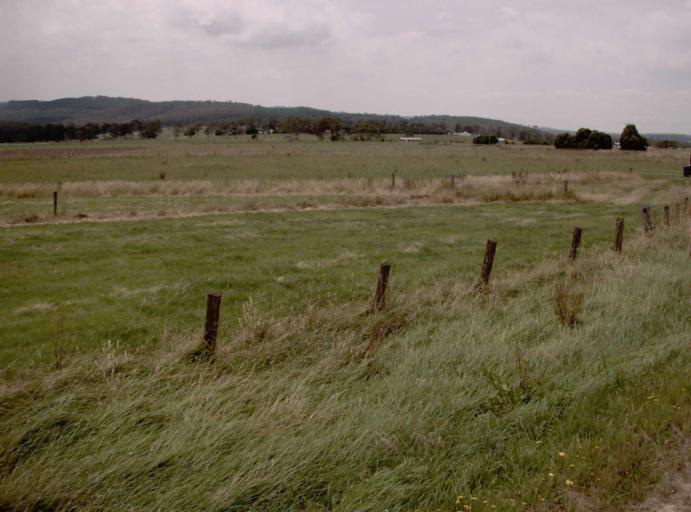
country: AU
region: Victoria
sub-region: Latrobe
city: Traralgon
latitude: -38.4978
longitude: 146.6771
